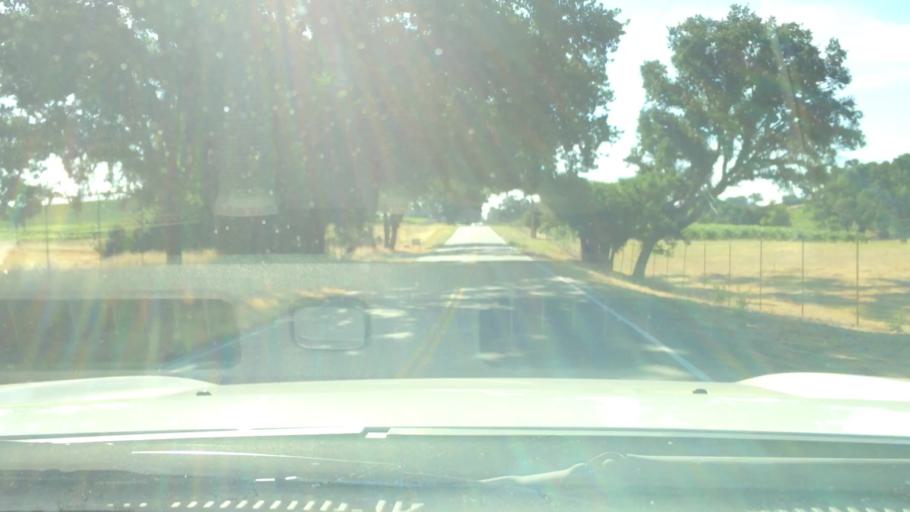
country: US
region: California
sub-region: San Luis Obispo County
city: Atascadero
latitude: 35.5553
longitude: -120.6233
